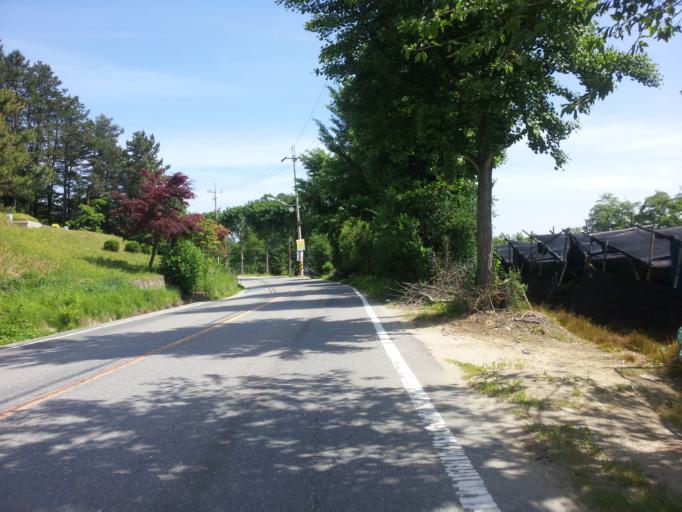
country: KR
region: Daejeon
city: Daejeon
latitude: 36.3399
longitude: 127.4787
